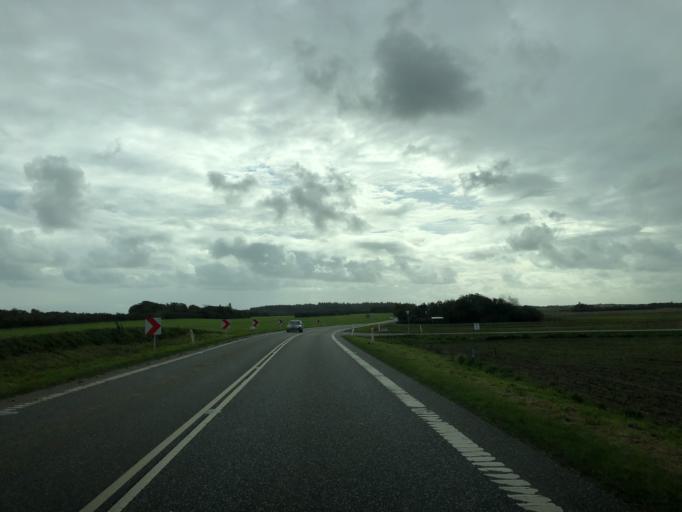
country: DK
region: North Denmark
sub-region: Thisted Kommune
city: Hurup
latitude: 56.7275
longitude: 8.4280
